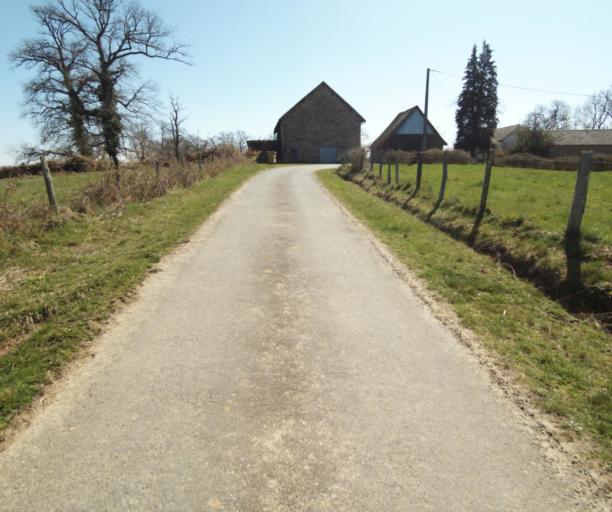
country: FR
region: Limousin
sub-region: Departement de la Correze
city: Saint-Clement
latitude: 45.3076
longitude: 1.6994
